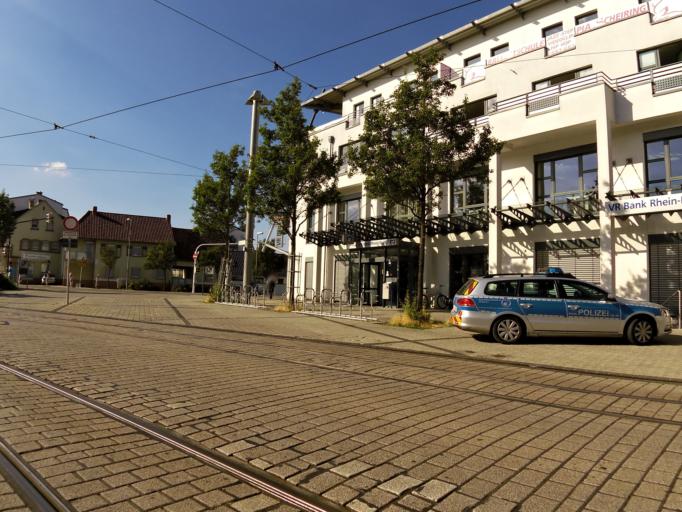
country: DE
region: Rheinland-Pfalz
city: Gartenstadt
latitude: 49.4928
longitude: 8.3759
